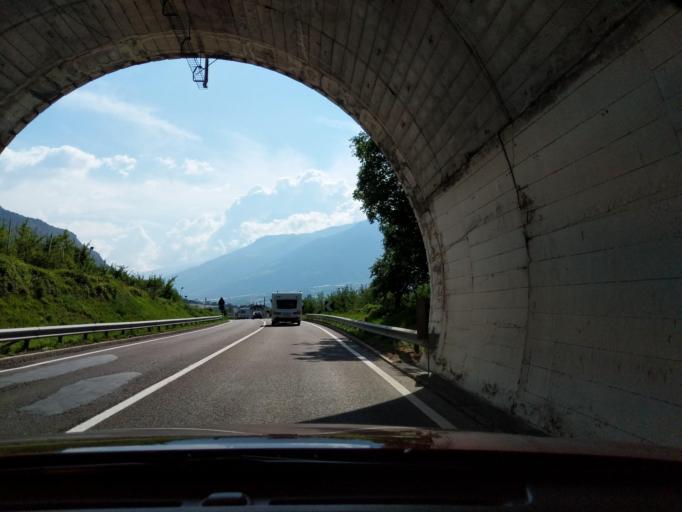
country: IT
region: Trentino-Alto Adige
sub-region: Bolzano
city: Laces
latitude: 46.6212
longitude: 10.8201
